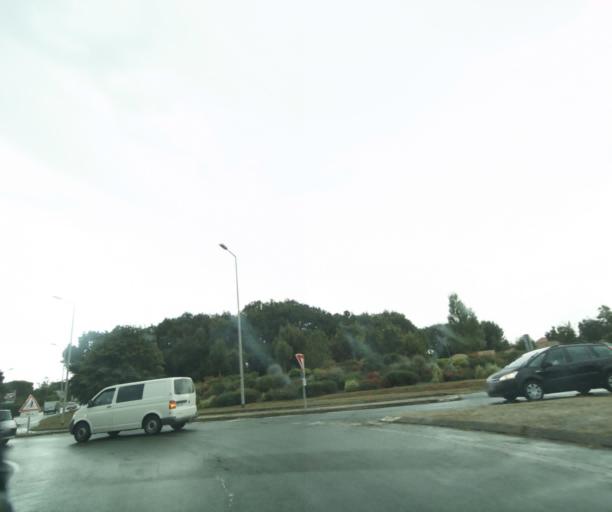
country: FR
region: Poitou-Charentes
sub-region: Departement de la Charente-Maritime
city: Tonnay-Charente
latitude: 45.9502
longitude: -0.8960
